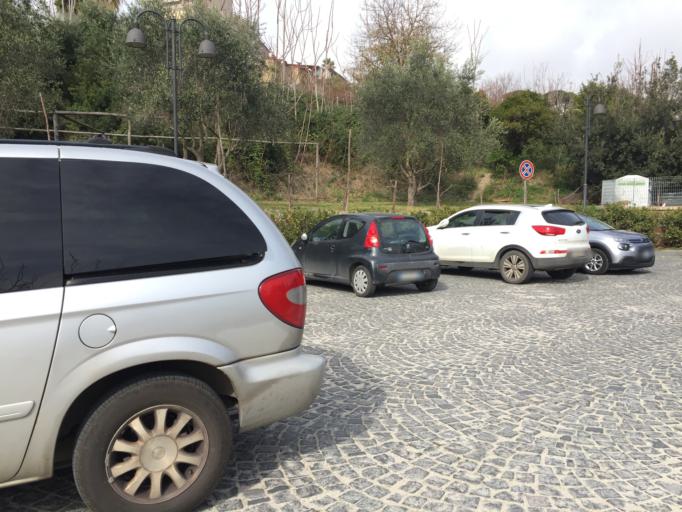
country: IT
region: Campania
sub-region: Provincia di Napoli
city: Pozzuoli
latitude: 40.8320
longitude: 14.1297
